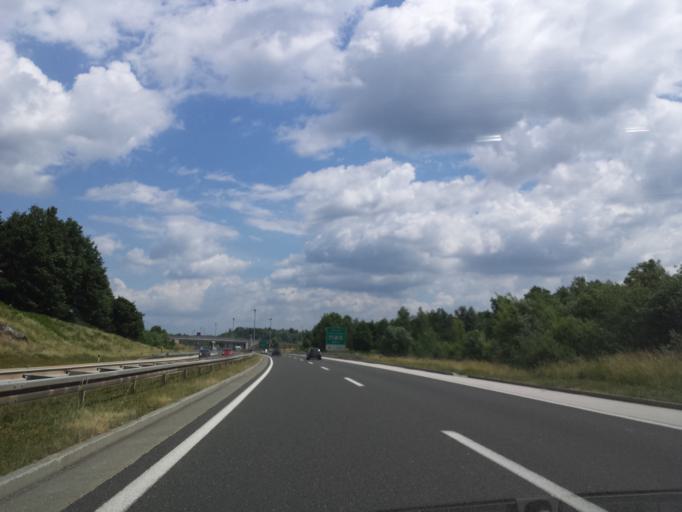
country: HR
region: Karlovacka
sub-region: Grad Karlovac
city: Karlovac
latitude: 45.4498
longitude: 15.3716
